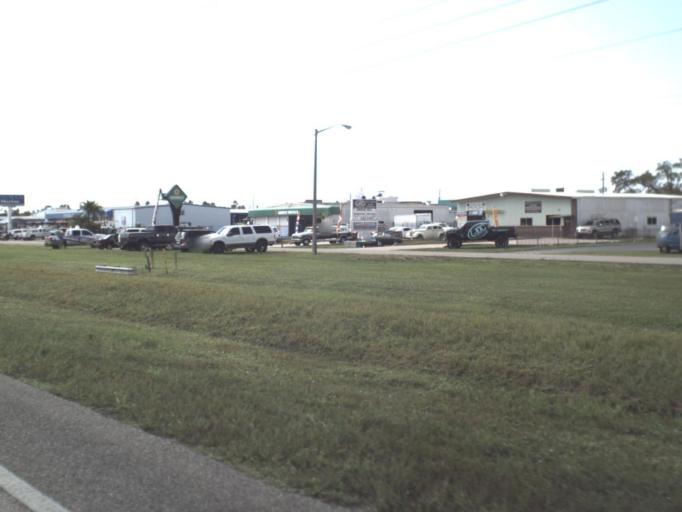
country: US
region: Florida
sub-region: Charlotte County
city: Port Charlotte
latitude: 27.0153
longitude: -82.1517
